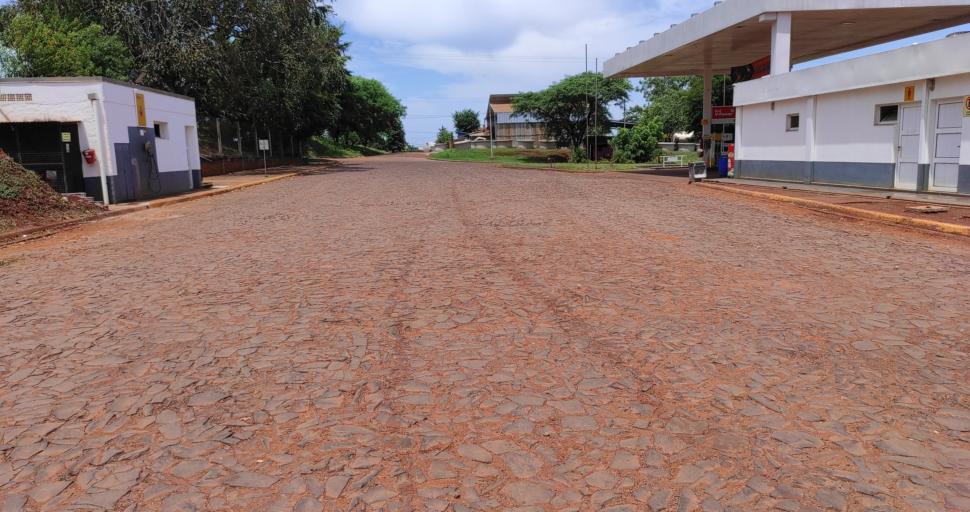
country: AR
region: Misiones
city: Puerto Esperanza
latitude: -26.0187
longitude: -54.5848
